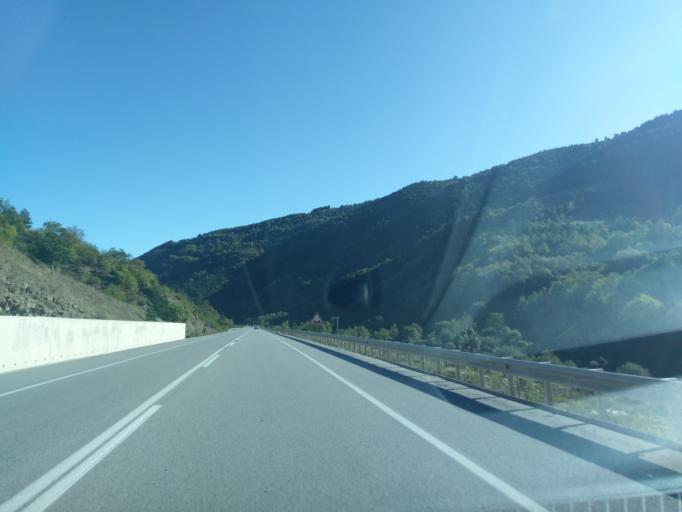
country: TR
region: Sinop
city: Erfelek
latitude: 41.7107
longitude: 34.9263
